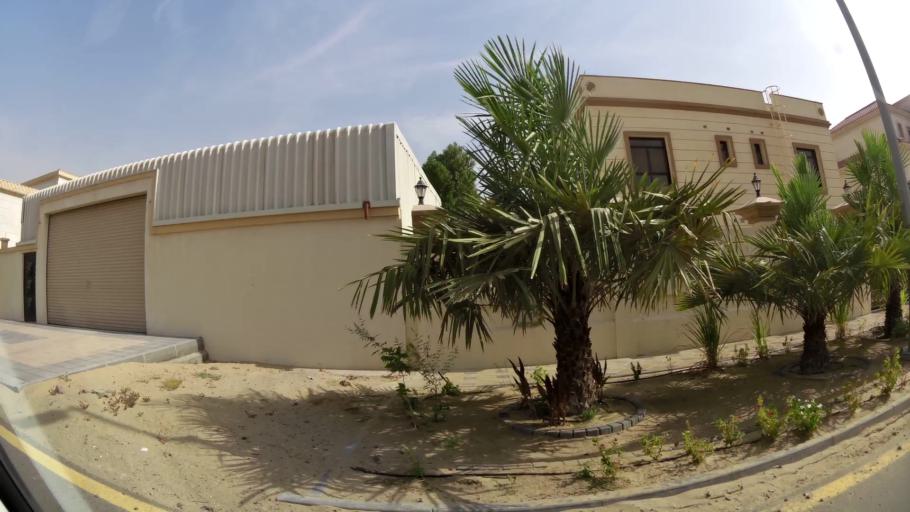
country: AE
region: Ash Shariqah
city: Sharjah
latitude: 25.2580
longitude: 55.4583
